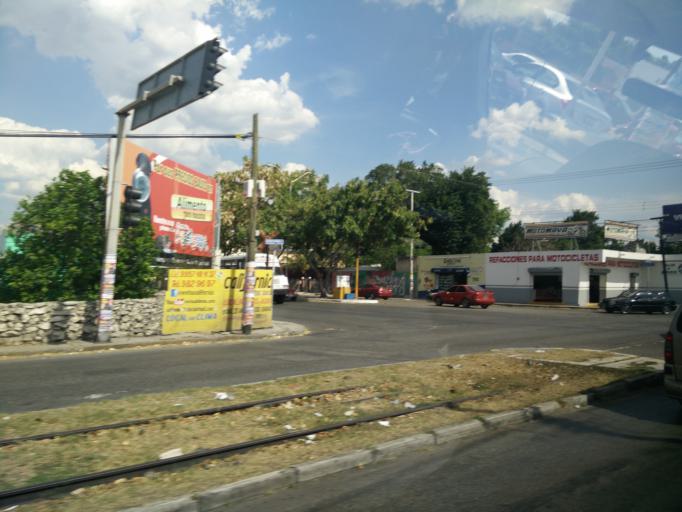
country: MX
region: Yucatan
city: Merida
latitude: 20.9656
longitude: -89.5915
